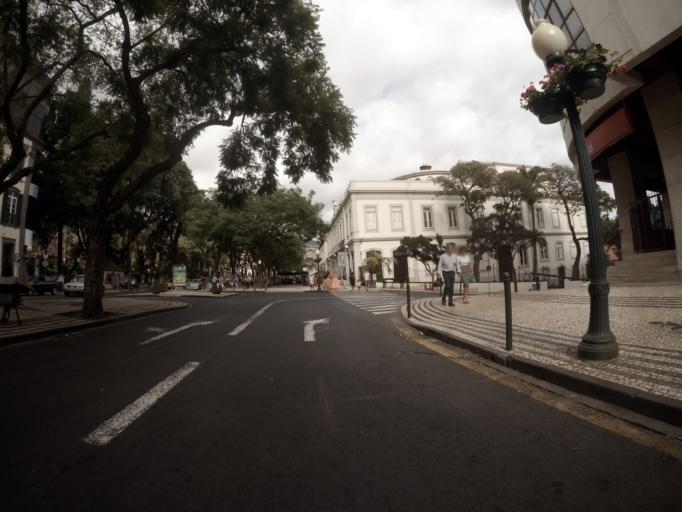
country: PT
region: Madeira
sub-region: Funchal
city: Funchal
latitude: 32.6470
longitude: -16.9120
